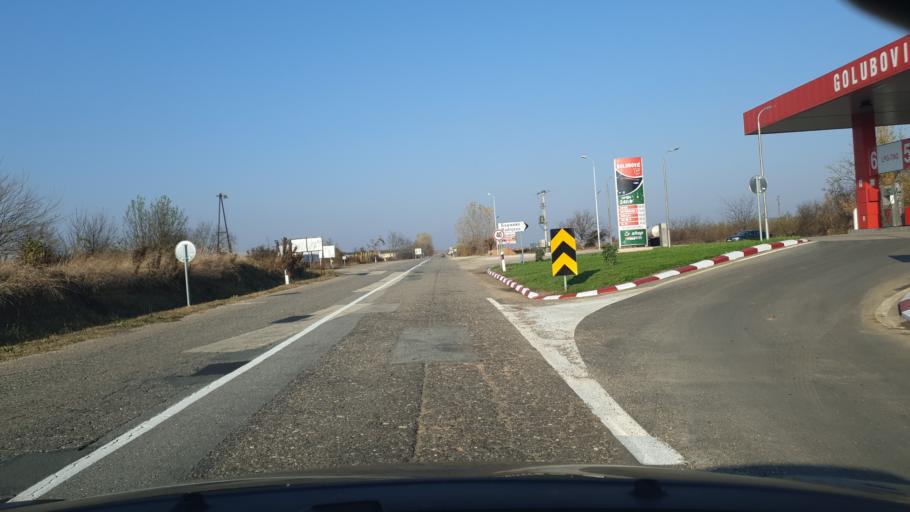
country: RS
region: Central Serbia
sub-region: Borski Okrug
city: Negotin
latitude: 44.2407
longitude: 22.5158
